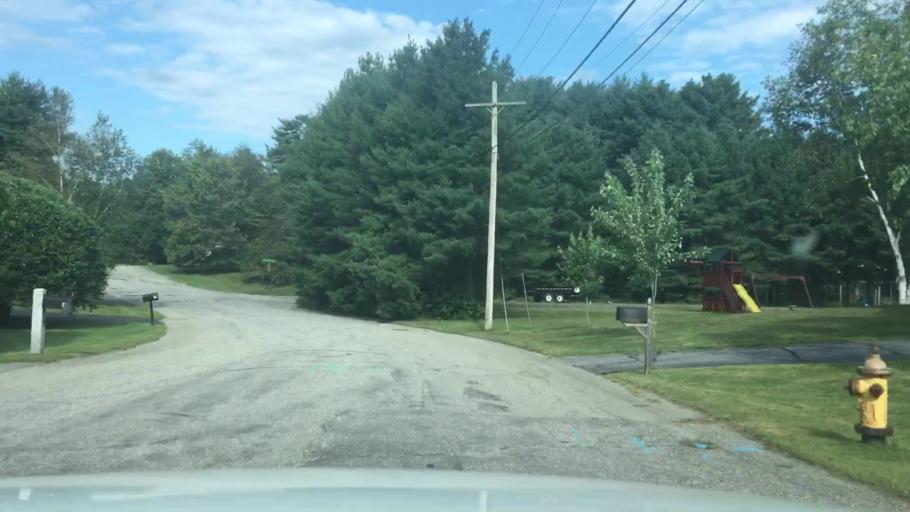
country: US
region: Maine
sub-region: Androscoggin County
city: Lewiston
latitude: 44.1163
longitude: -70.2002
